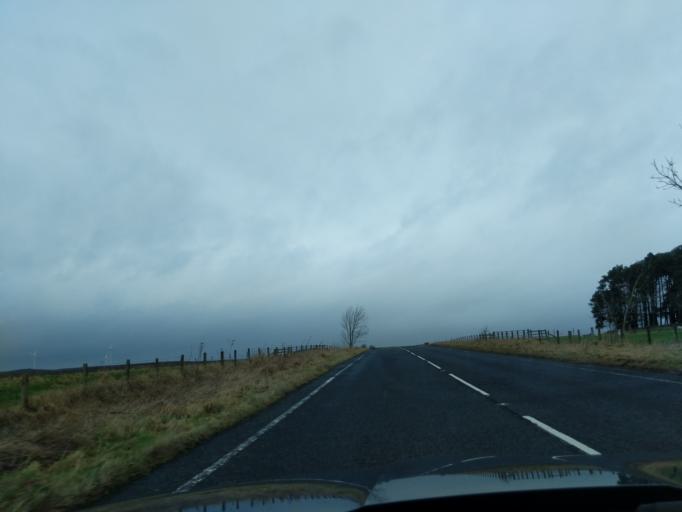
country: GB
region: England
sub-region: Northumberland
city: Rothley
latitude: 55.1695
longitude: -2.0225
